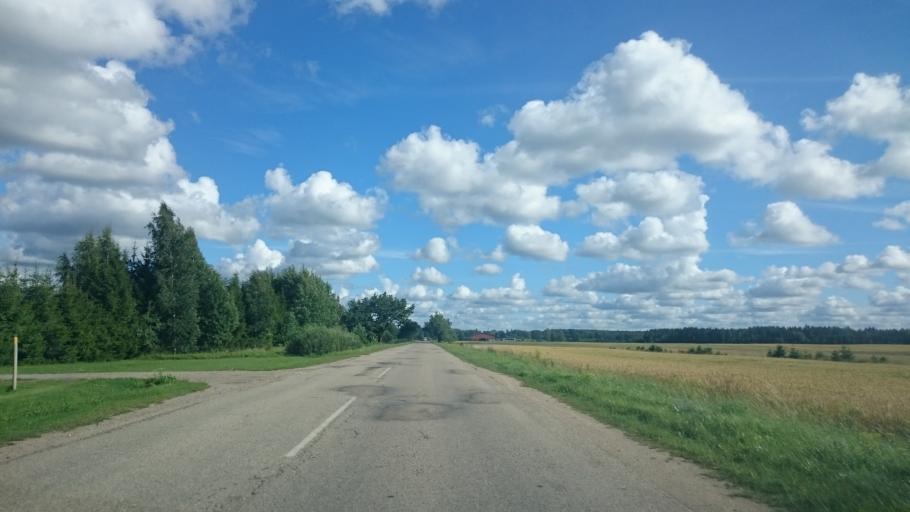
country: LV
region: Aizpute
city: Aizpute
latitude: 56.7035
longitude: 21.6263
